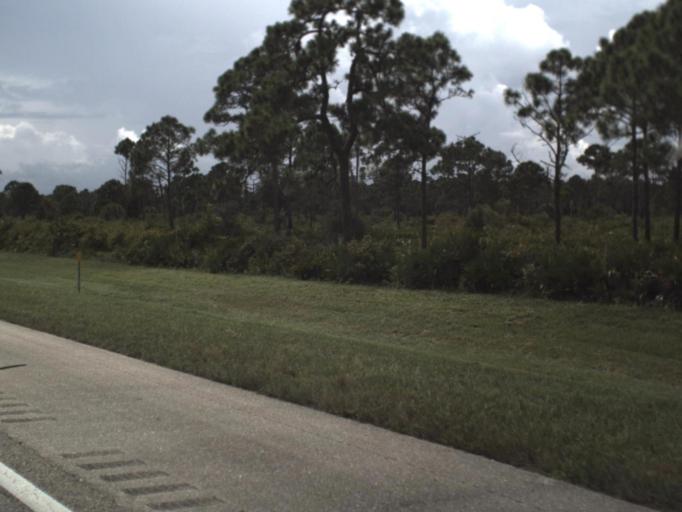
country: US
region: Florida
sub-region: Sarasota County
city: Laurel
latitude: 27.1728
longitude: -82.4528
